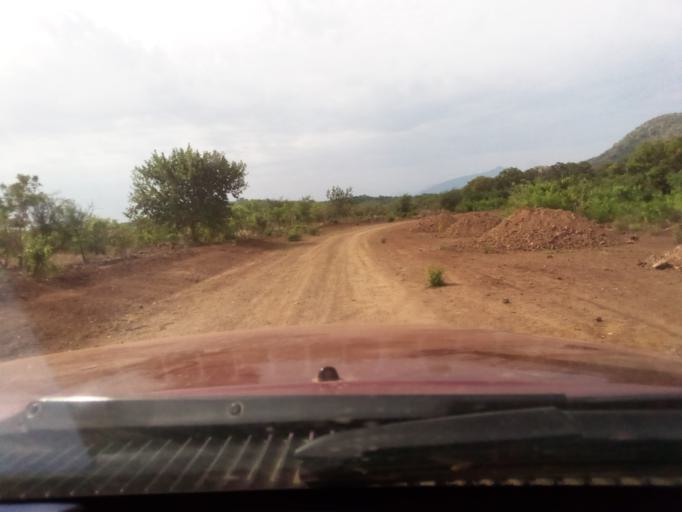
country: ET
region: Oromiya
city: Mendi
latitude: 10.0432
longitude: 35.3056
